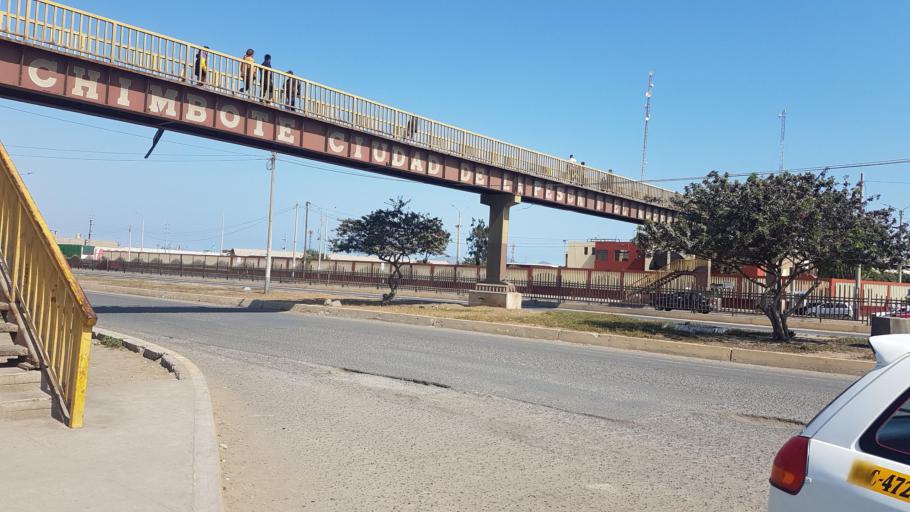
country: PE
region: Ancash
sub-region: Provincia de Santa
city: Chimbote
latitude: -9.1036
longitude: -78.5575
